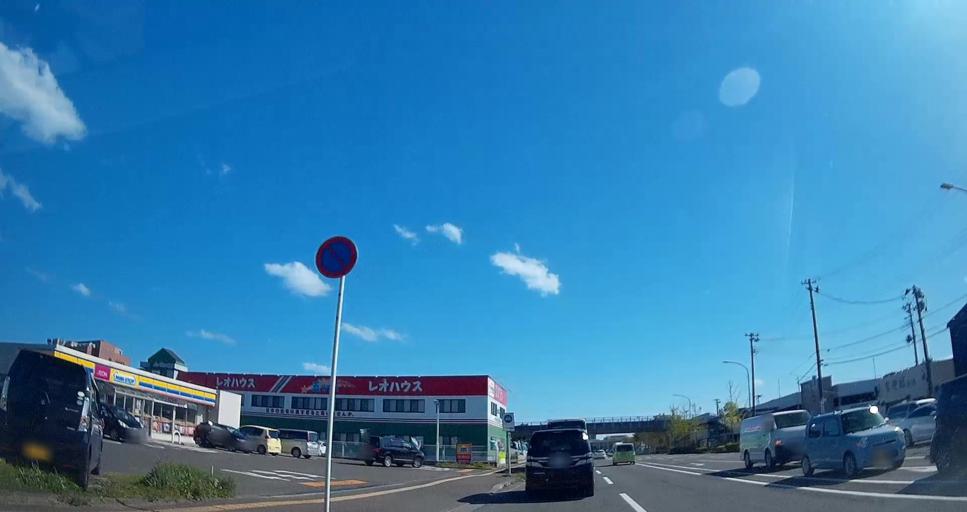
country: JP
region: Miyagi
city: Sendai-shi
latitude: 38.2501
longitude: 140.9522
